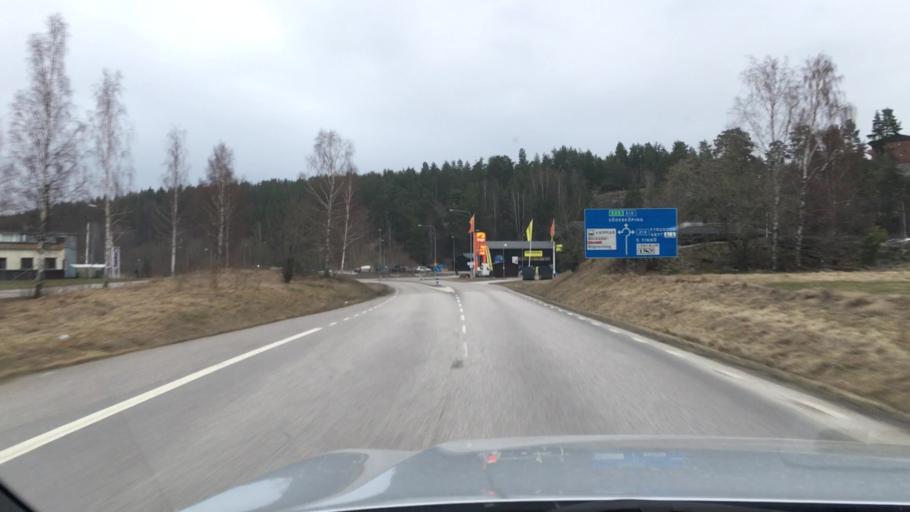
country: SE
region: OEstergoetland
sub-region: Valdemarsviks Kommun
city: Valdemarsvik
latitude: 58.2100
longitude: 16.5840
